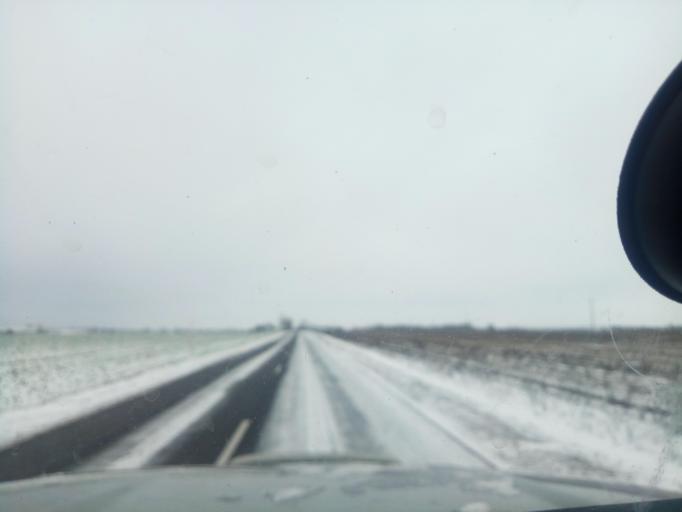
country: BY
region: Minsk
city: Klyetsk
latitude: 53.0520
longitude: 26.7629
